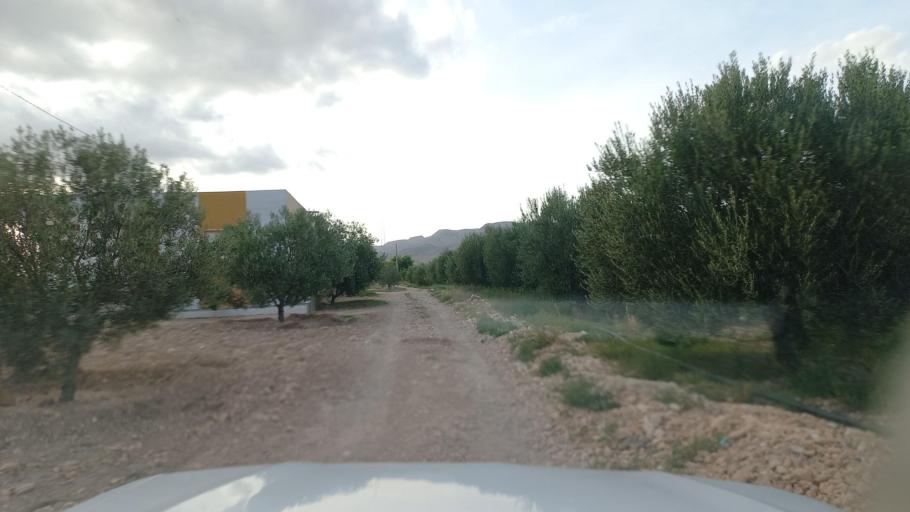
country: TN
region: Al Qasrayn
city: Sbiba
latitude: 35.4374
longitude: 9.0939
